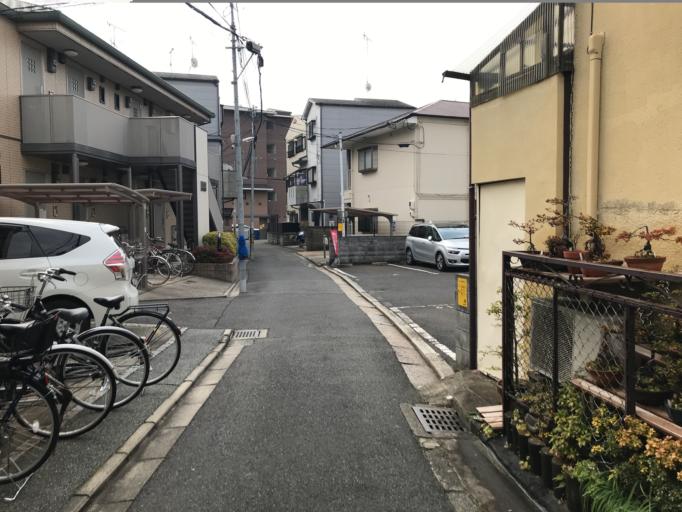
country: JP
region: Kyoto
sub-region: Kyoto-shi
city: Kamigyo-ku
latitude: 35.0277
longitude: 135.7765
